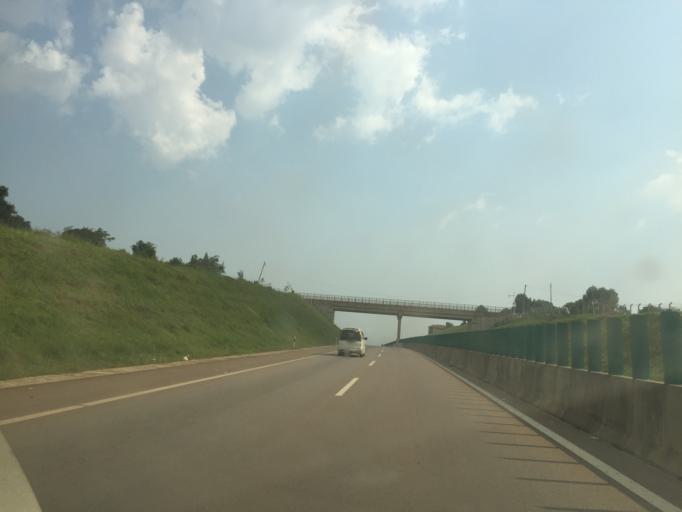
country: UG
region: Central Region
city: Kampala Central Division
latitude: 0.2831
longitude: 32.5125
